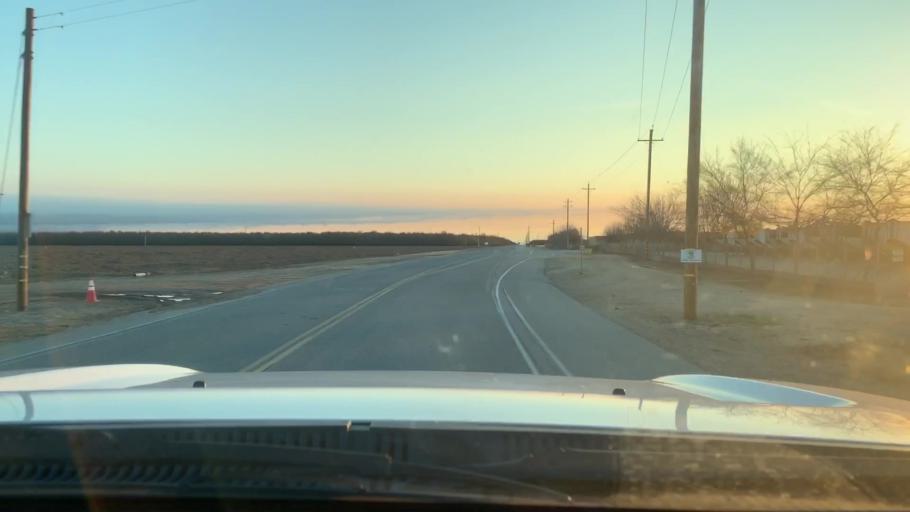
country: US
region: California
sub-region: Kern County
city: Buttonwillow
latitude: 35.5008
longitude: -119.5284
